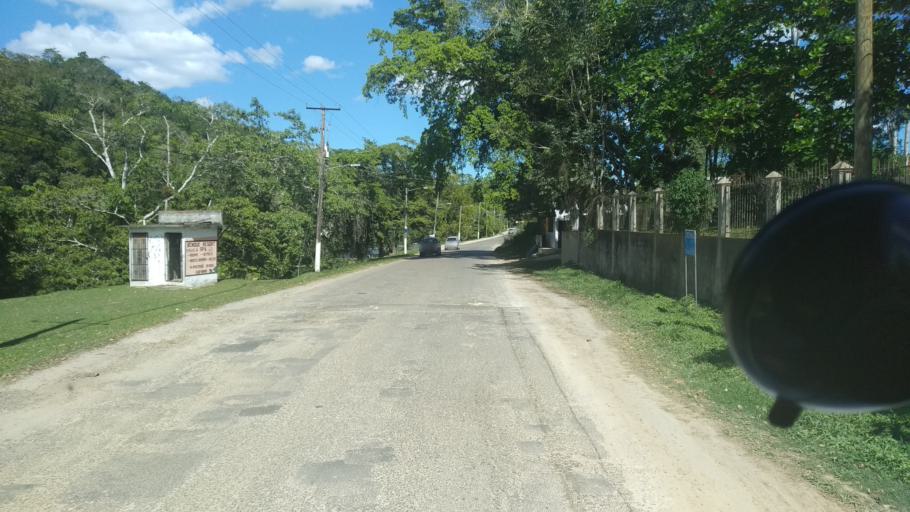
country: BZ
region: Cayo
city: Benque Viejo del Carmen
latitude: 17.0859
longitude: -89.1326
